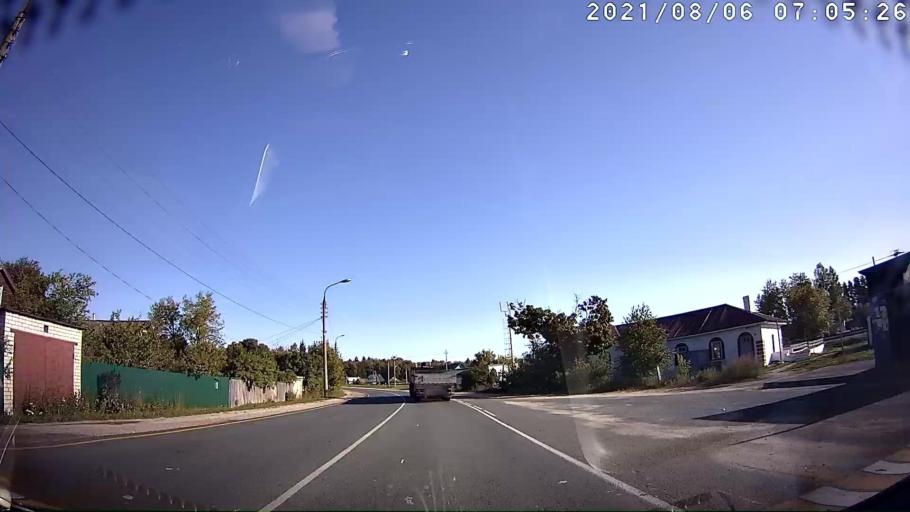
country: RU
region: Mariy-El
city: Yoshkar-Ola
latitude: 56.5534
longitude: 47.9866
